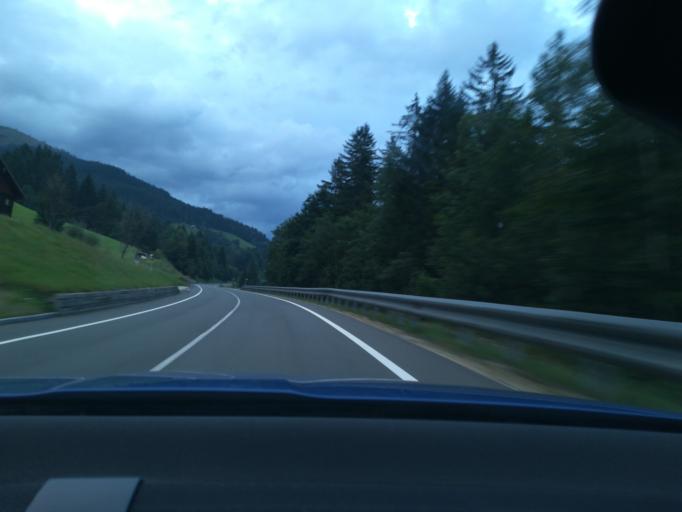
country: AT
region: Salzburg
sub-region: Politischer Bezirk Salzburg-Umgebung
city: Strobl
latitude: 47.5924
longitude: 13.4761
